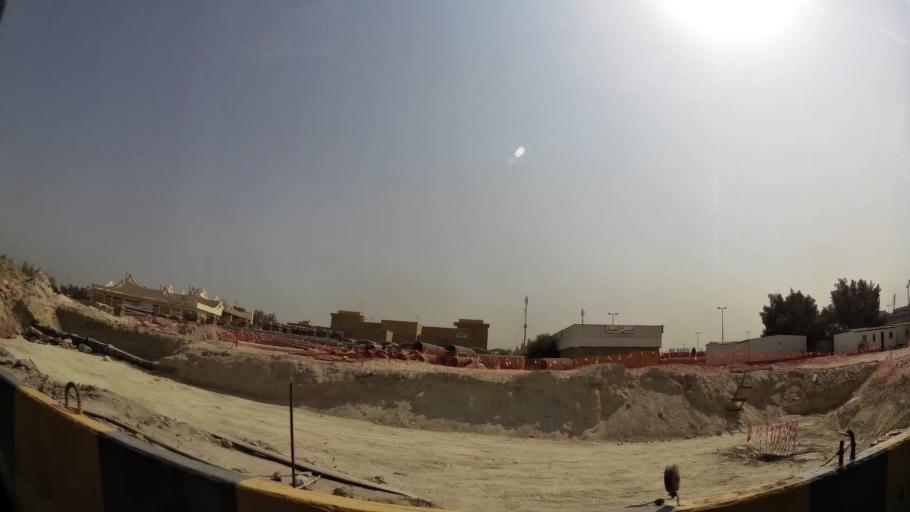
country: KW
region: Al Asimah
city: Ash Shamiyah
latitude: 29.3469
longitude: 47.9545
